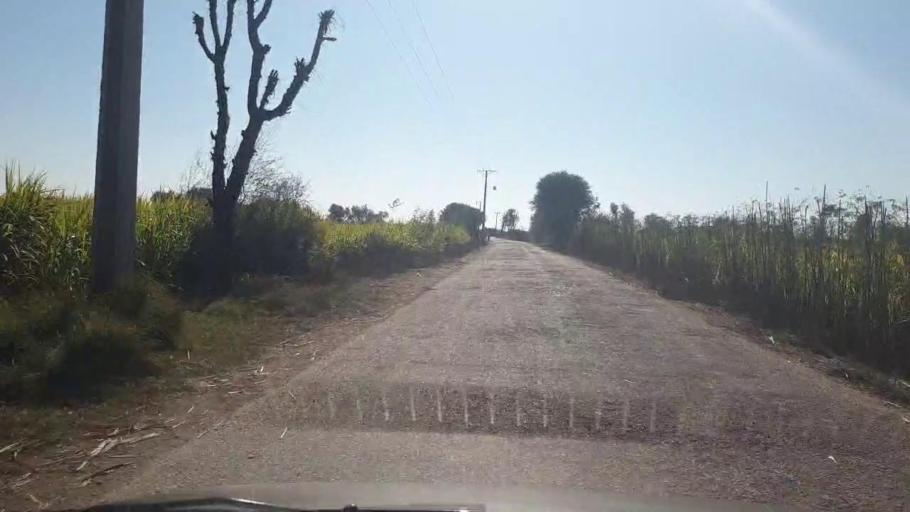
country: PK
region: Sindh
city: Bozdar
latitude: 27.2650
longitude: 68.6525
